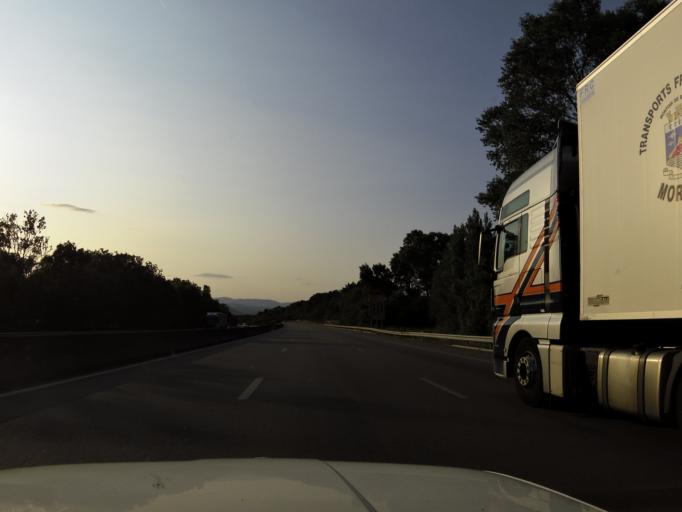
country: FR
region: Rhone-Alpes
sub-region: Departement de la Drome
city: Beausemblant
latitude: 45.2223
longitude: 4.8583
